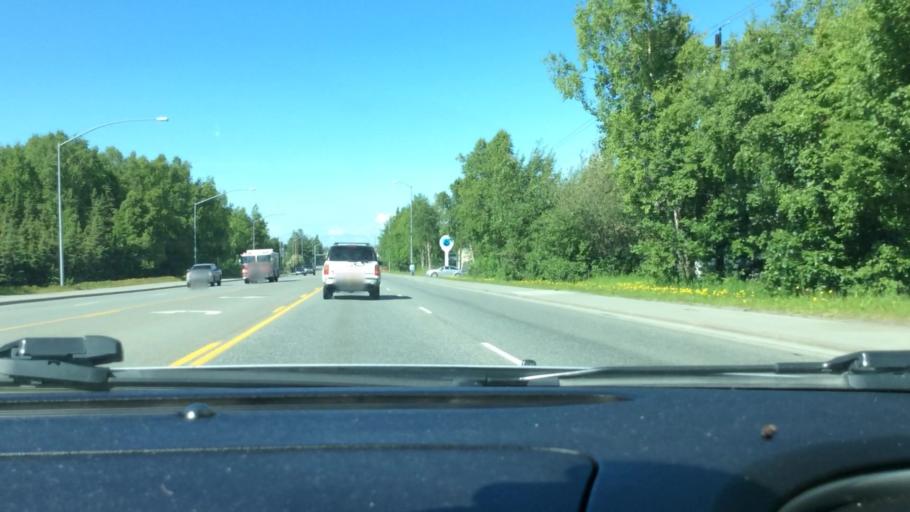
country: US
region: Alaska
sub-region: Anchorage Municipality
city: Anchorage
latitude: 61.2141
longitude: -149.7784
